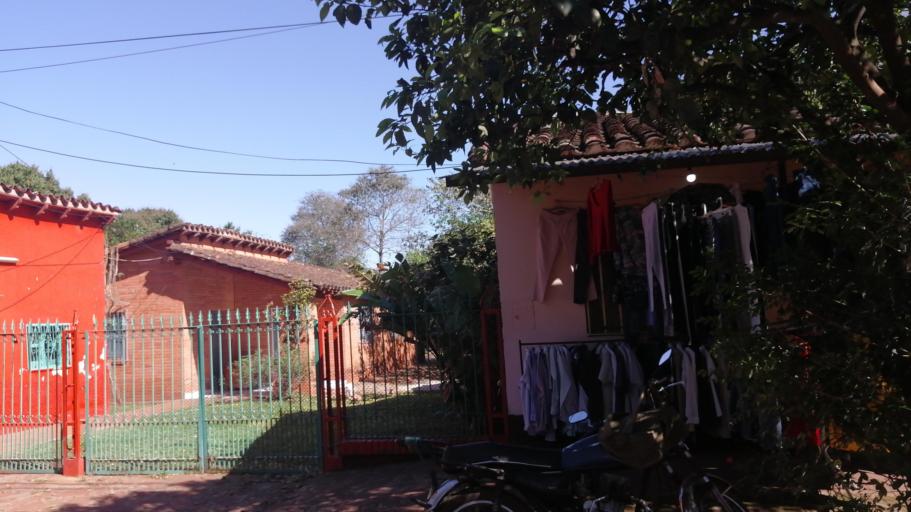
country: PY
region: Misiones
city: San Juan Bautista
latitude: -26.6720
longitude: -57.1415
